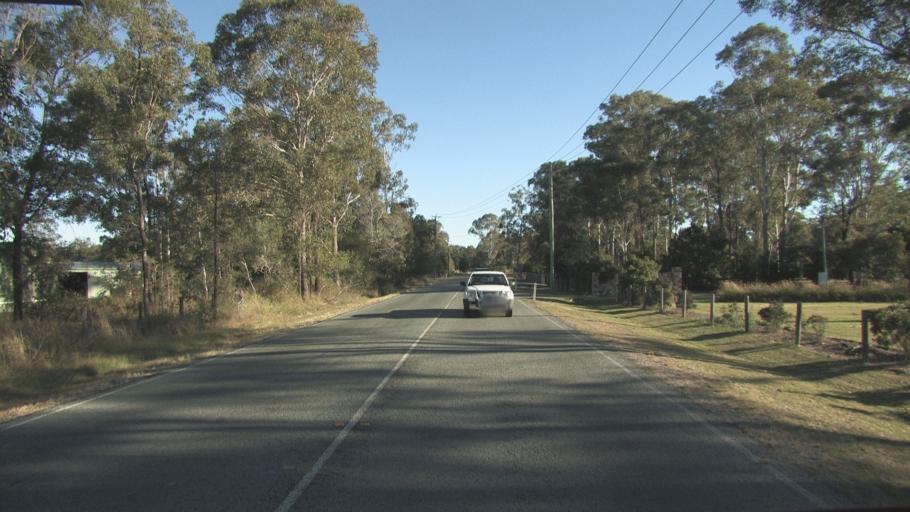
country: AU
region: Queensland
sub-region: Logan
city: Chambers Flat
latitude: -27.7471
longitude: 153.0598
